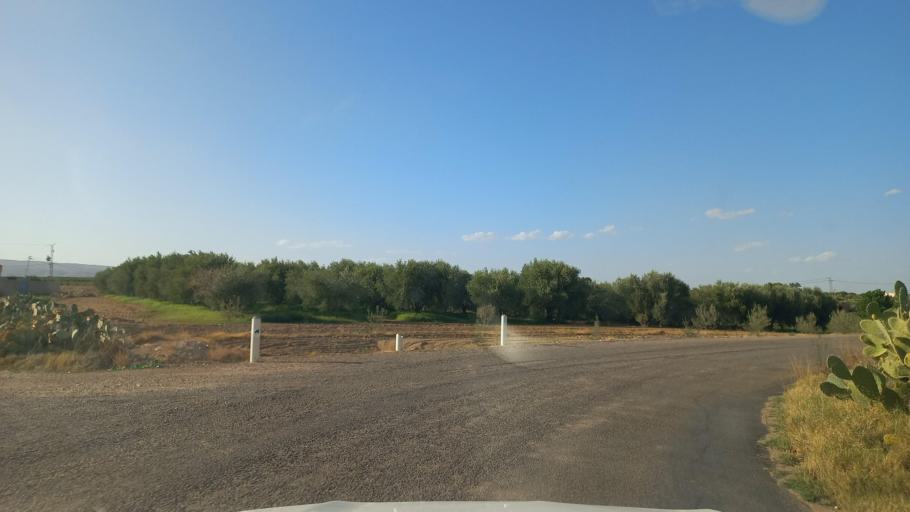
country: TN
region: Al Qasrayn
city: Kasserine
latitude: 35.2665
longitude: 9.0273
